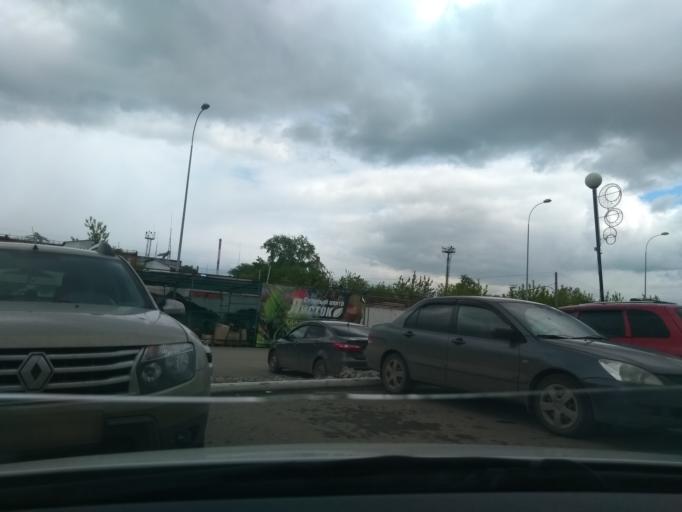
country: RU
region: Perm
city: Perm
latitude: 57.9814
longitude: 56.2414
